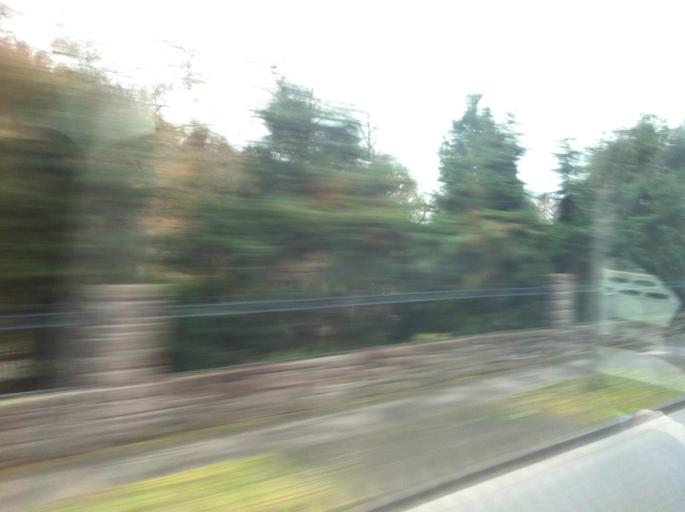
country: DE
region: Rheinland-Pfalz
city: Bad Munster am Stein-Ebernburg
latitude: 49.8290
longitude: 7.8472
